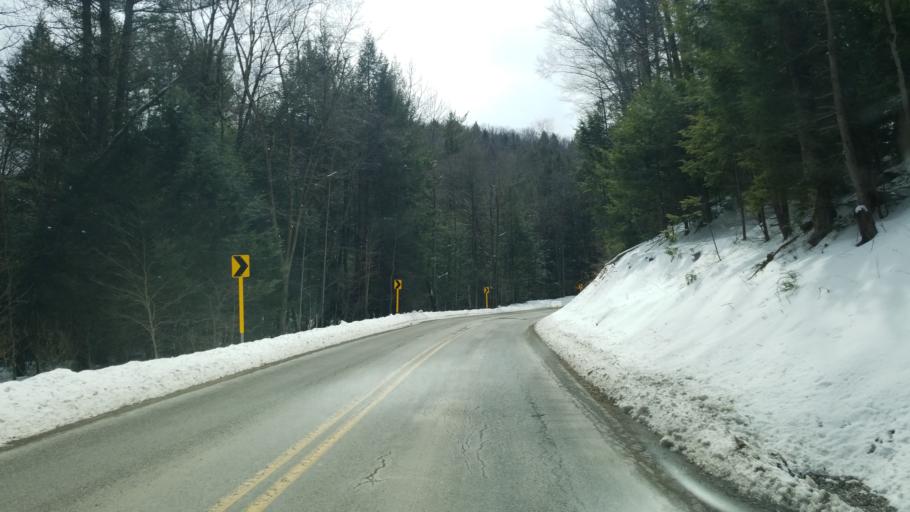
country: US
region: Pennsylvania
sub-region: Clearfield County
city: Shiloh
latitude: 41.2494
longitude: -78.1522
